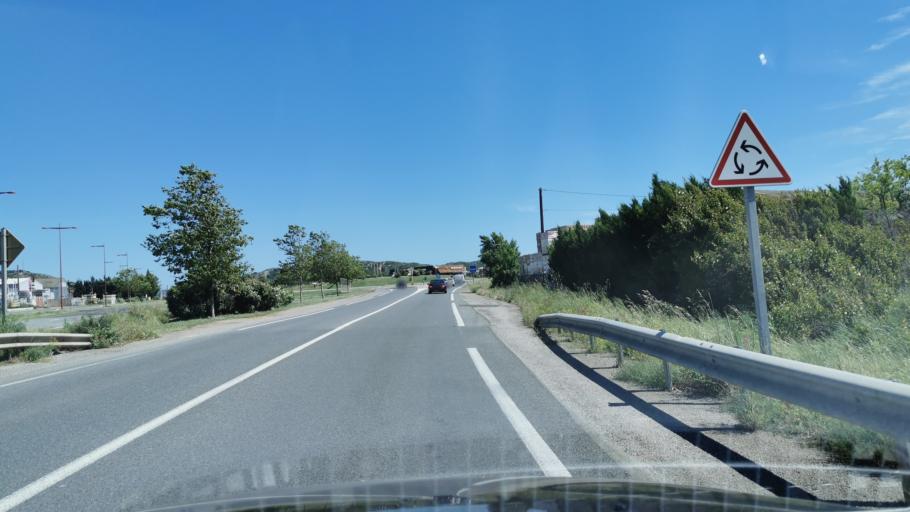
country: FR
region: Languedoc-Roussillon
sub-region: Departement de l'Aude
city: Nevian
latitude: 43.1847
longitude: 2.9317
